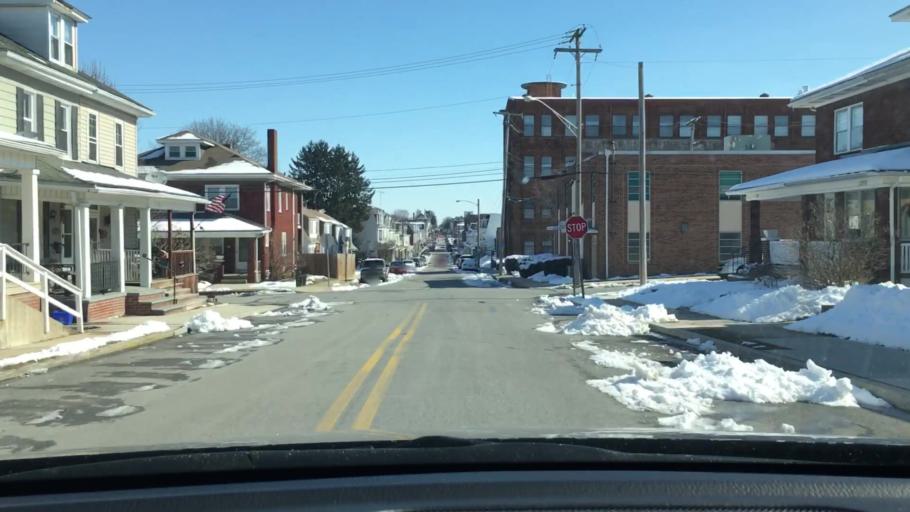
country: US
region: Pennsylvania
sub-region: York County
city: West York
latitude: 39.9520
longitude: -76.7537
